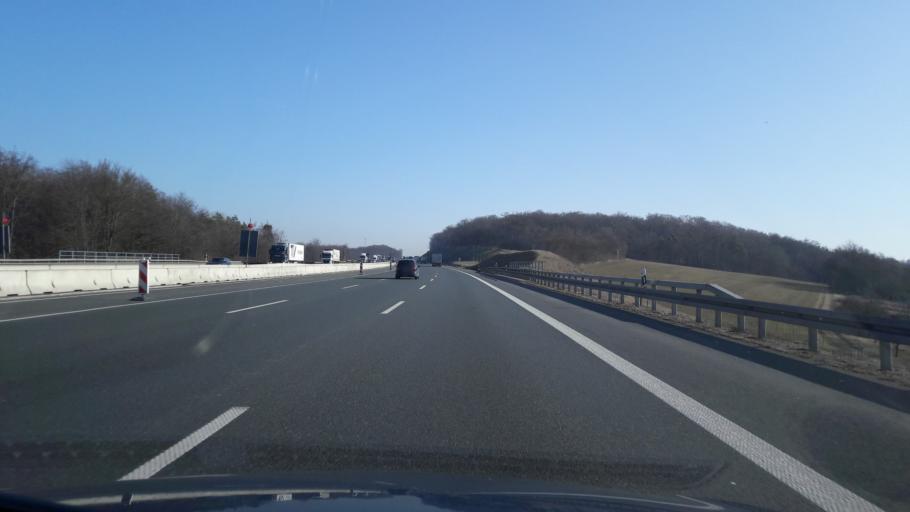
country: DE
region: Bavaria
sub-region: Regierungsbezirk Unterfranken
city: Helmstadt
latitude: 49.7684
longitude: 9.6928
